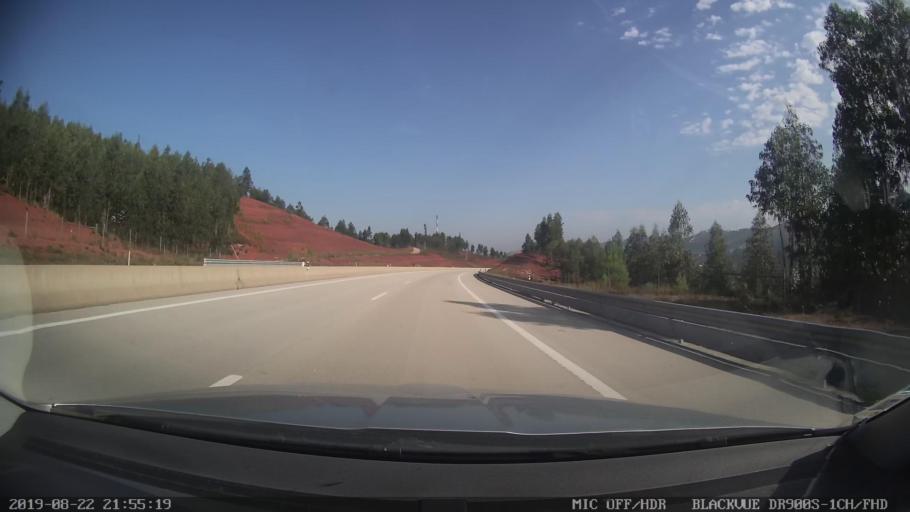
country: PT
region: Coimbra
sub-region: Coimbra
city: Coimbra
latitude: 40.1516
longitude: -8.3849
